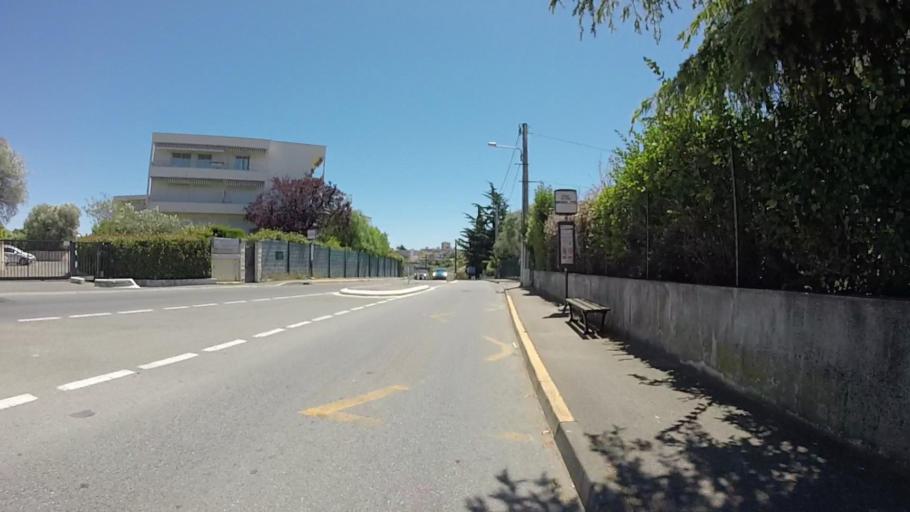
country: FR
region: Provence-Alpes-Cote d'Azur
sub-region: Departement des Alpes-Maritimes
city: Antibes
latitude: 43.5852
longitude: 7.0982
